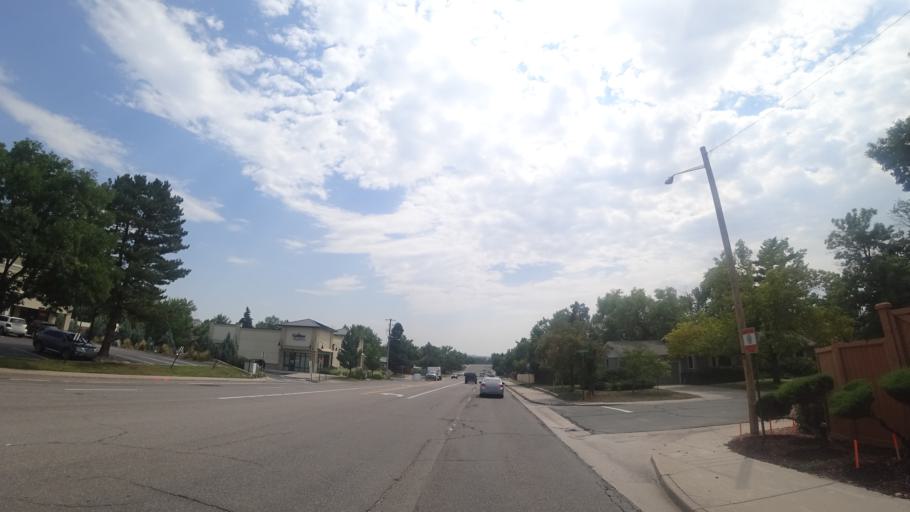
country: US
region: Colorado
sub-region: Arapahoe County
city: Greenwood Village
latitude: 39.6081
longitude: -104.9601
